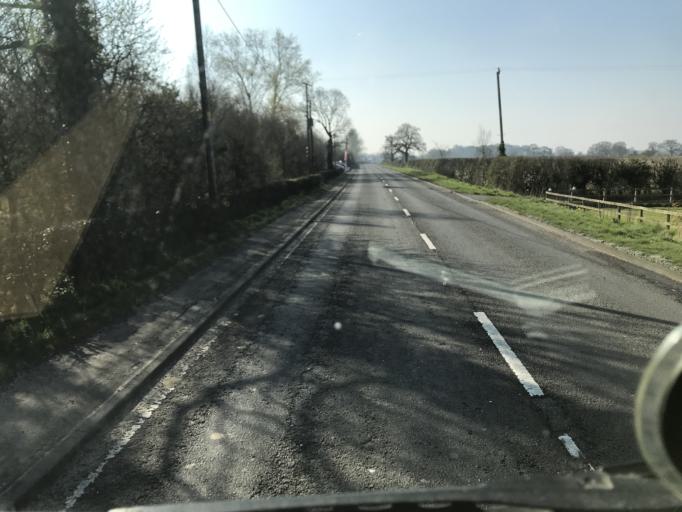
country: GB
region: England
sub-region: Cheshire West and Chester
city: Waverton
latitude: 53.1518
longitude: -2.8120
